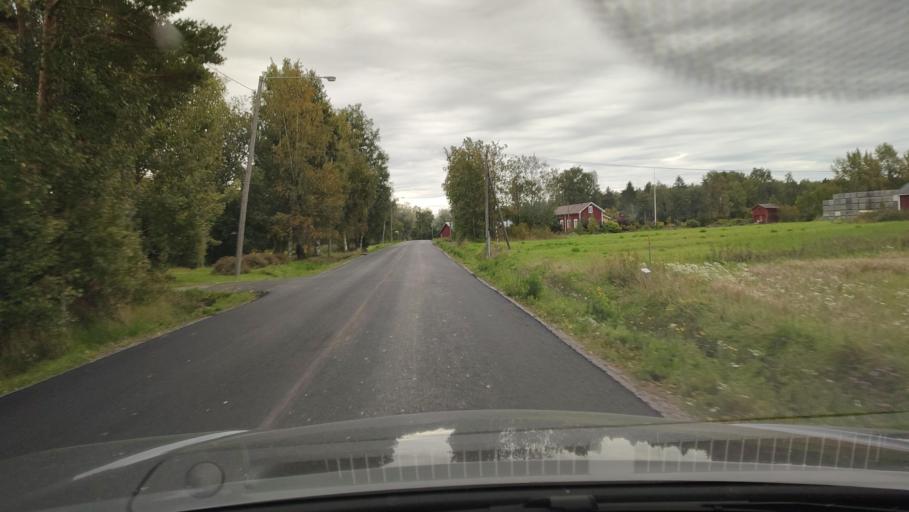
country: FI
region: Ostrobothnia
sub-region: Sydosterbotten
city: Kristinestad
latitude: 62.2502
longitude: 21.5228
